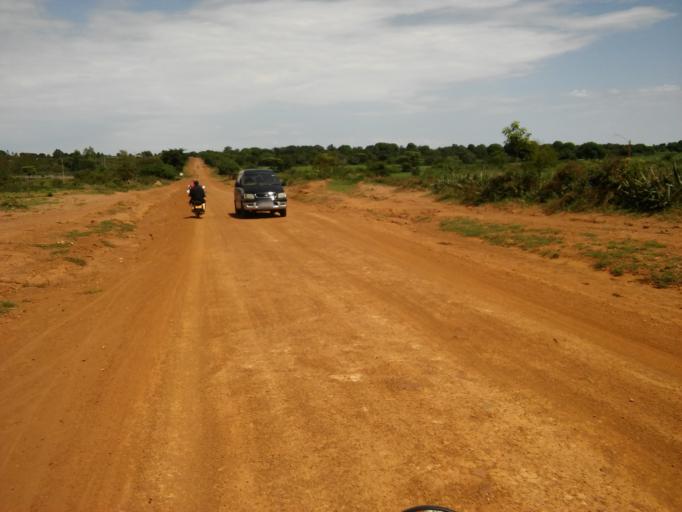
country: UG
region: Eastern Region
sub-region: Kumi District
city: Kumi
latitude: 1.4811
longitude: 33.8992
